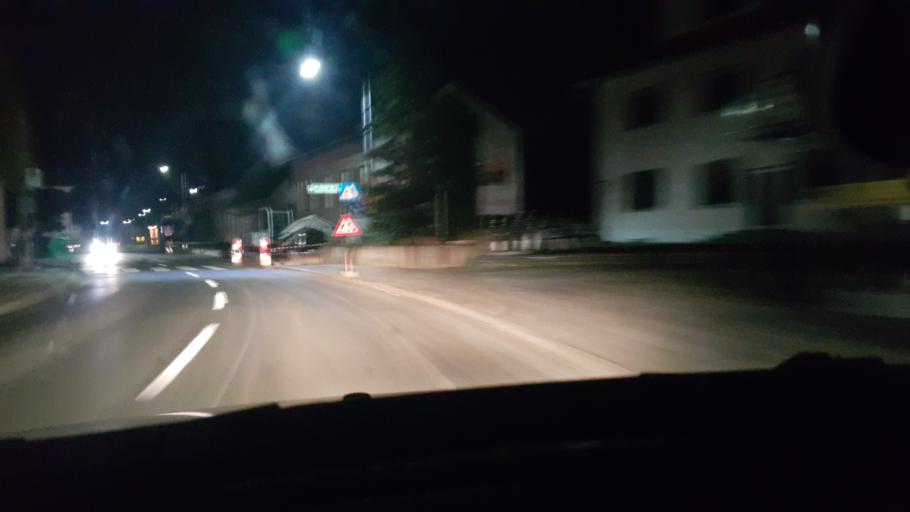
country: AT
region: Styria
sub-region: Politischer Bezirk Deutschlandsberg
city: Sankt Martin im Sulmtal
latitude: 46.7564
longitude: 15.2958
